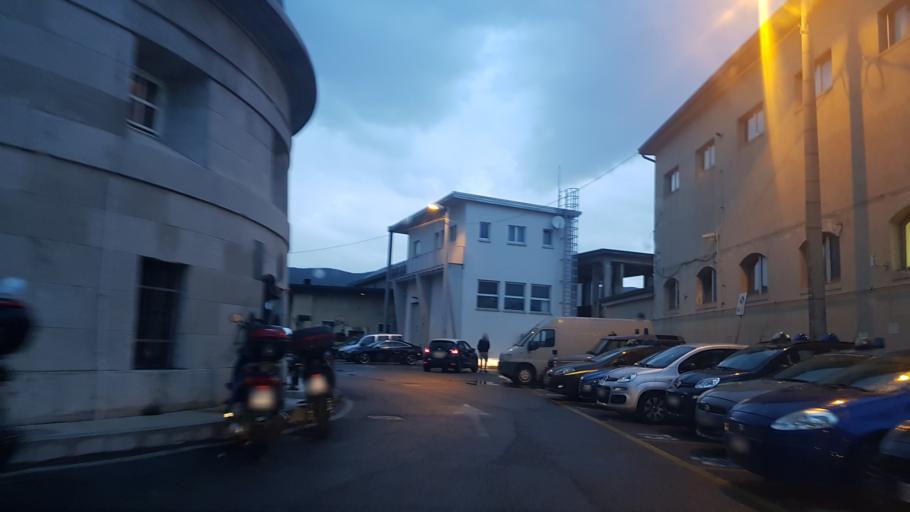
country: IT
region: Friuli Venezia Giulia
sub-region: Provincia di Trieste
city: Trieste
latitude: 45.6490
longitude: 13.7559
